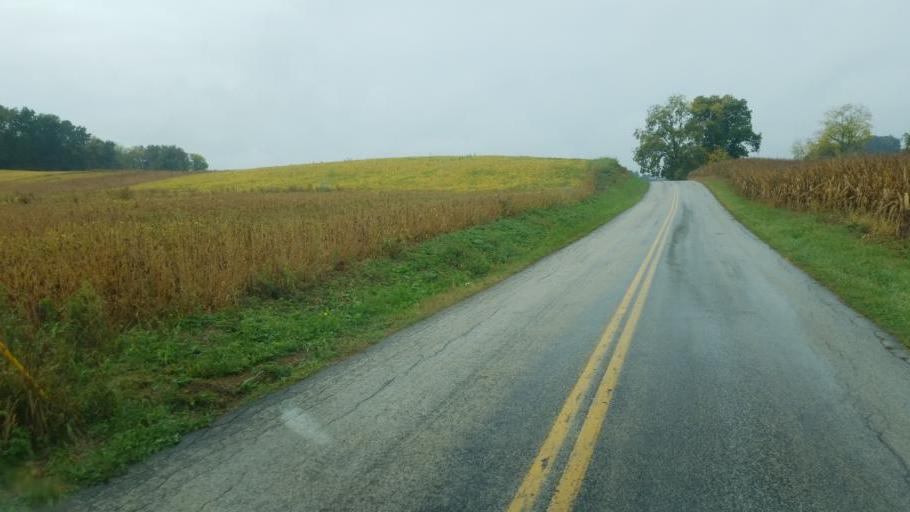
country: US
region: Ohio
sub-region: Sandusky County
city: Bellville
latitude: 40.6111
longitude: -82.4030
